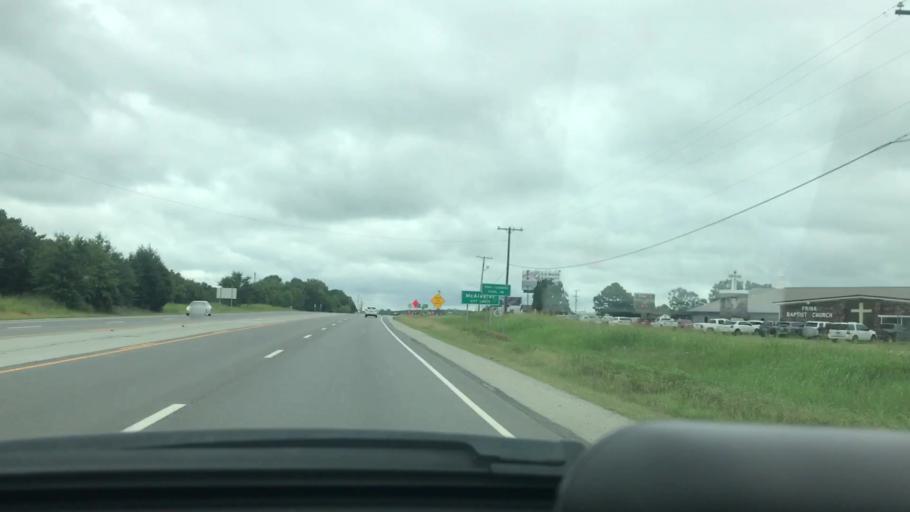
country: US
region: Oklahoma
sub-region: Pittsburg County
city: McAlester
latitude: 34.8831
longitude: -95.7915
